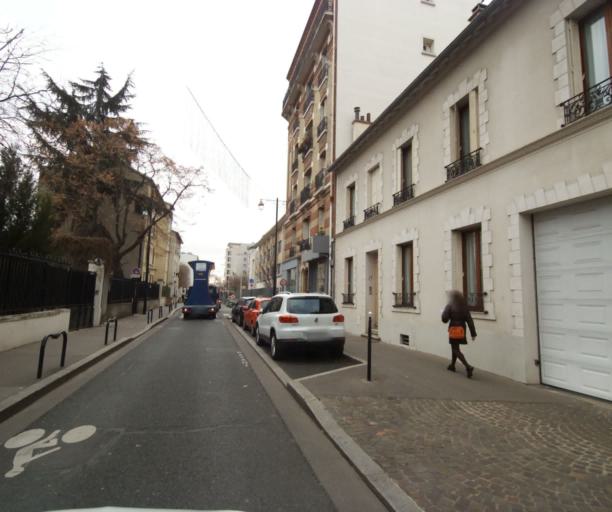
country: FR
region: Ile-de-France
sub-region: Departement des Hauts-de-Seine
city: Courbevoie
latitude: 48.9021
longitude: 2.2690
